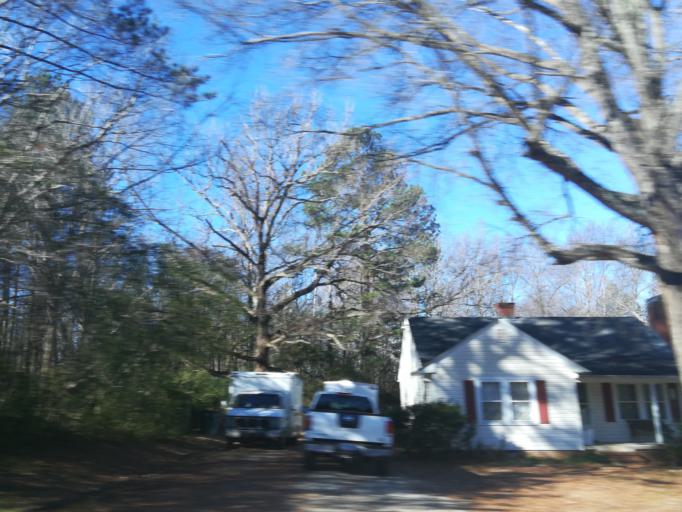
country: US
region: North Carolina
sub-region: Durham County
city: Durham
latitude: 36.0473
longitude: -78.9823
